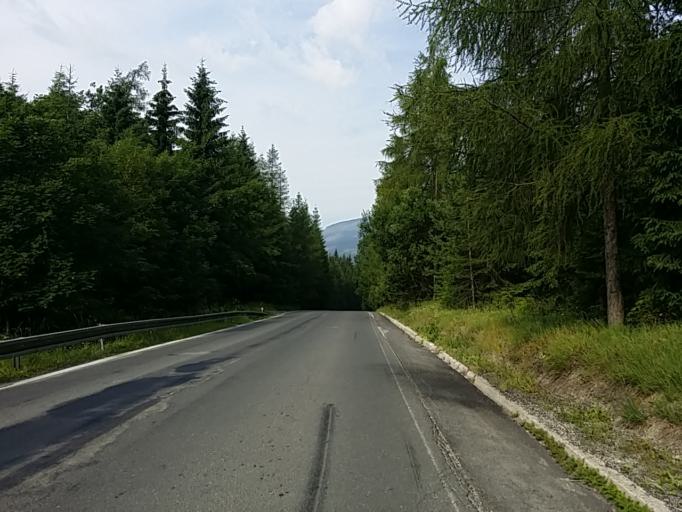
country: SK
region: Kosicky
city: Dobsina
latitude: 48.8919
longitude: 20.2458
